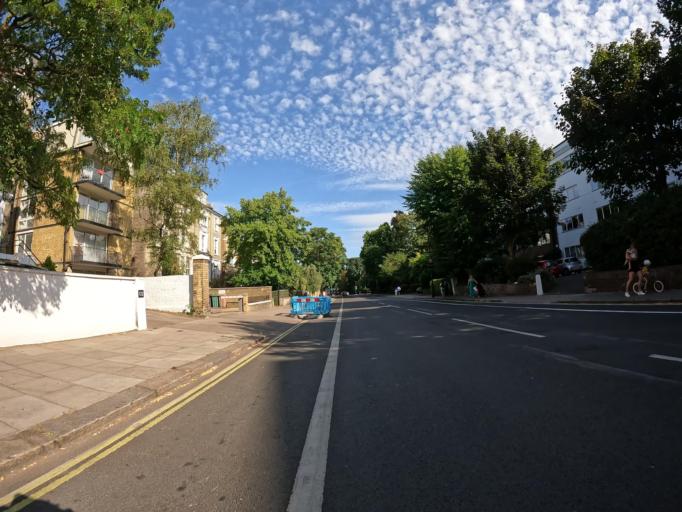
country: GB
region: England
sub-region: Greater London
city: Belsize Park
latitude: 51.5484
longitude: -0.1612
